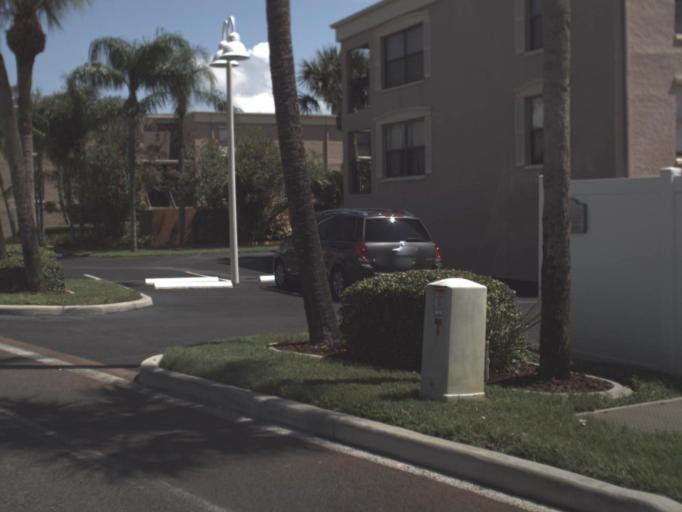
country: US
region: Florida
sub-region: Pinellas County
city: Indian Shores
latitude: 27.8585
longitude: -82.8470
